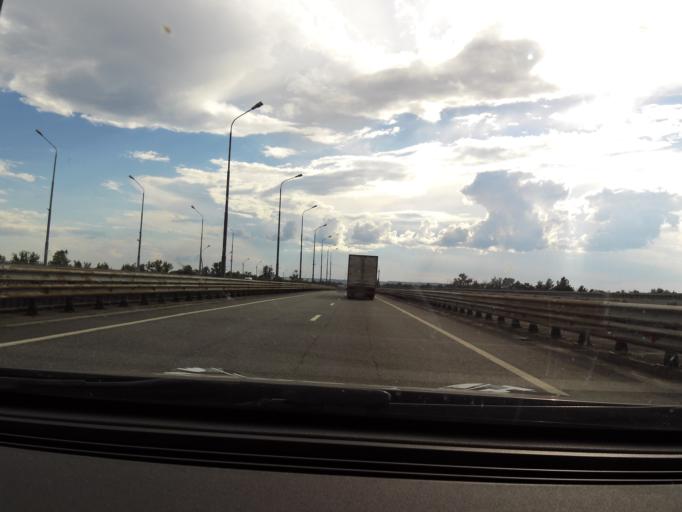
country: RU
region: Vladimir
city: Galitsy
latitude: 56.2230
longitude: 42.7798
